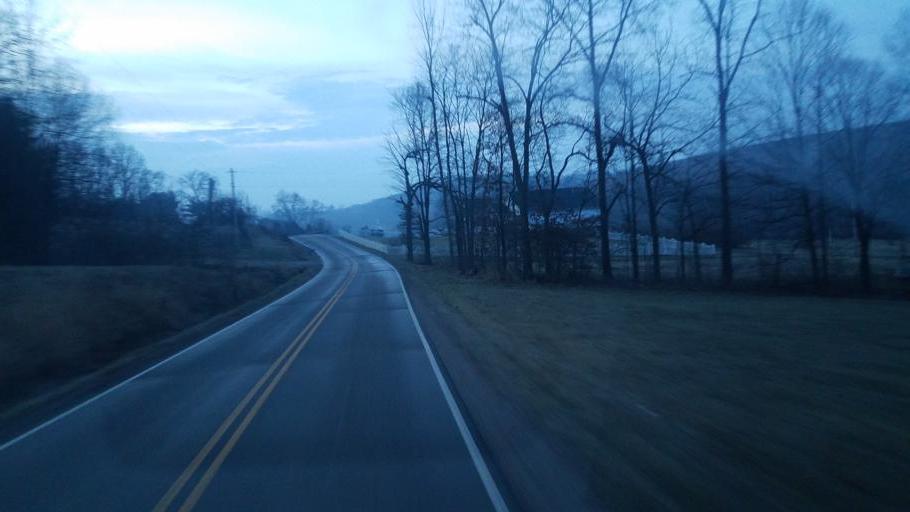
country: US
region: Ohio
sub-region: Coshocton County
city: West Lafayette
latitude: 40.3513
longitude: -81.7645
